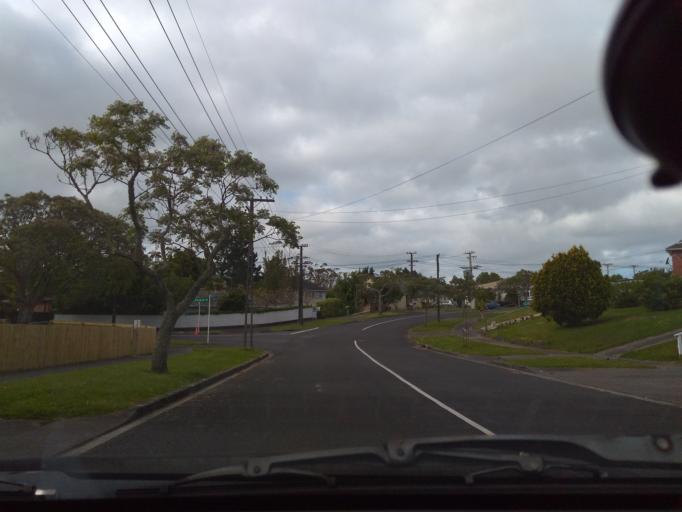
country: NZ
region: Auckland
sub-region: Auckland
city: Rosebank
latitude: -36.8762
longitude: 174.7145
